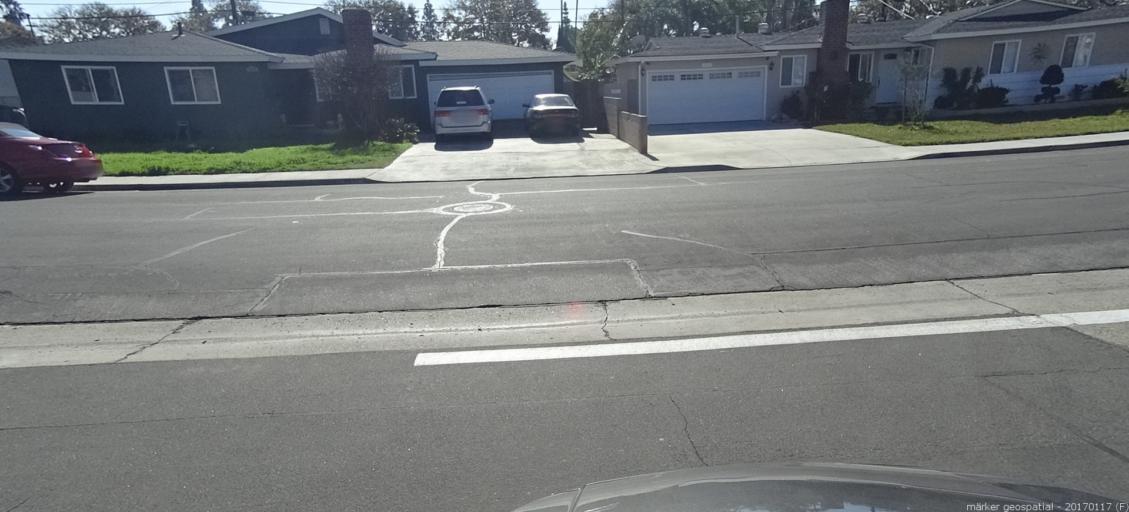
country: US
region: California
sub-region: Orange County
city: Stanton
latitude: 33.8219
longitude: -117.9619
